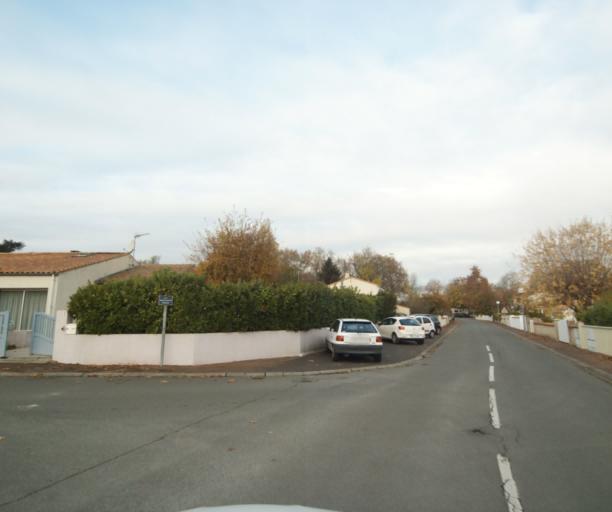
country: FR
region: Poitou-Charentes
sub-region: Departement de la Charente-Maritime
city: Saintes
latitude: 45.7506
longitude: -0.6504
